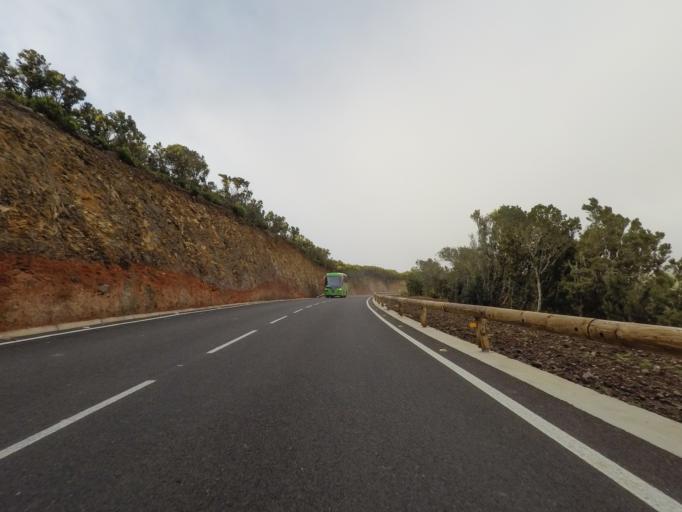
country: ES
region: Canary Islands
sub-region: Provincia de Santa Cruz de Tenerife
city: Vallehermosa
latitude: 28.1476
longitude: -17.3085
